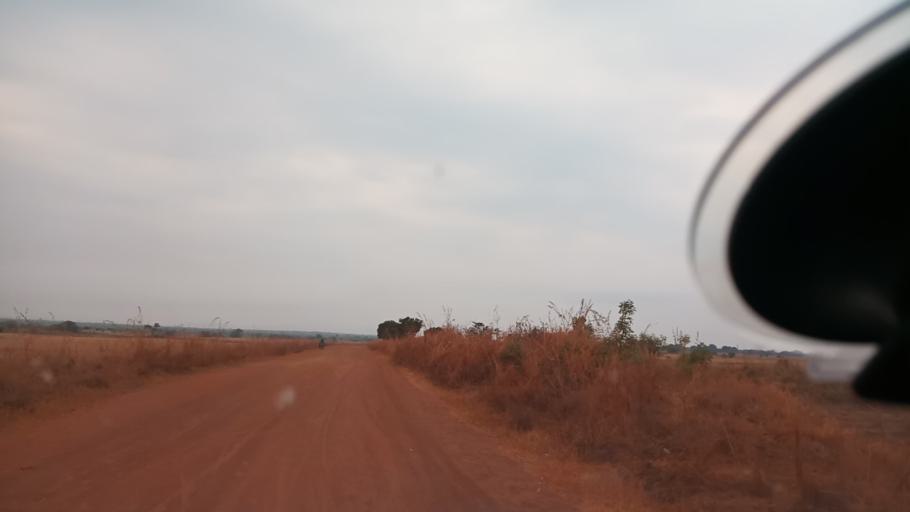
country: ZM
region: Luapula
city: Nchelenge
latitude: -9.2754
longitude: 28.3177
